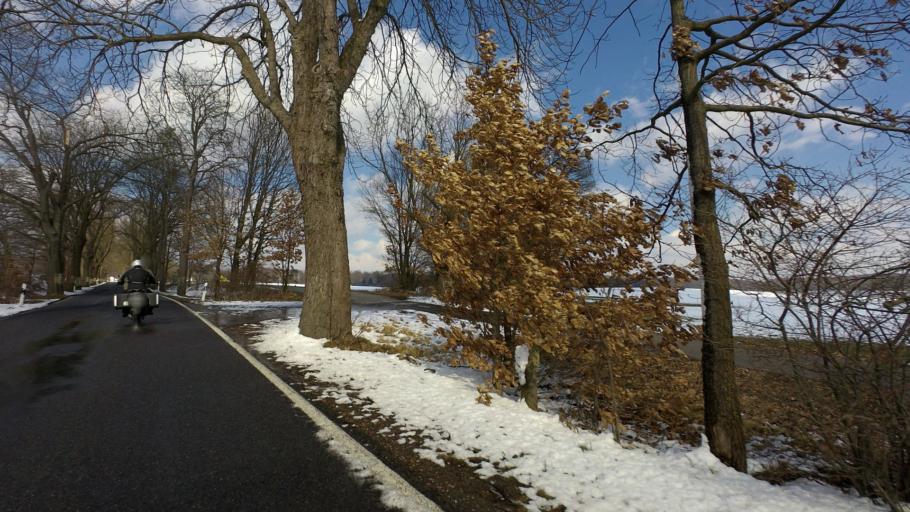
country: DE
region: Brandenburg
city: Joachimsthal
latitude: 52.9031
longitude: 13.7110
